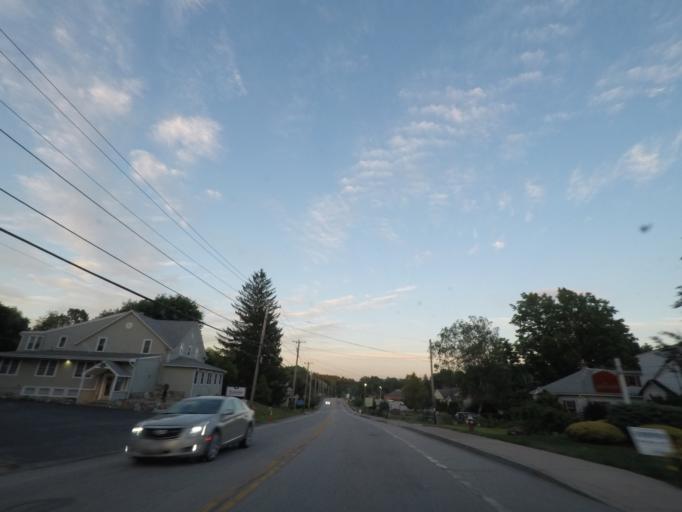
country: US
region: Massachusetts
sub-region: Worcester County
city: Sturbridge
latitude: 42.0884
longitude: -72.0645
